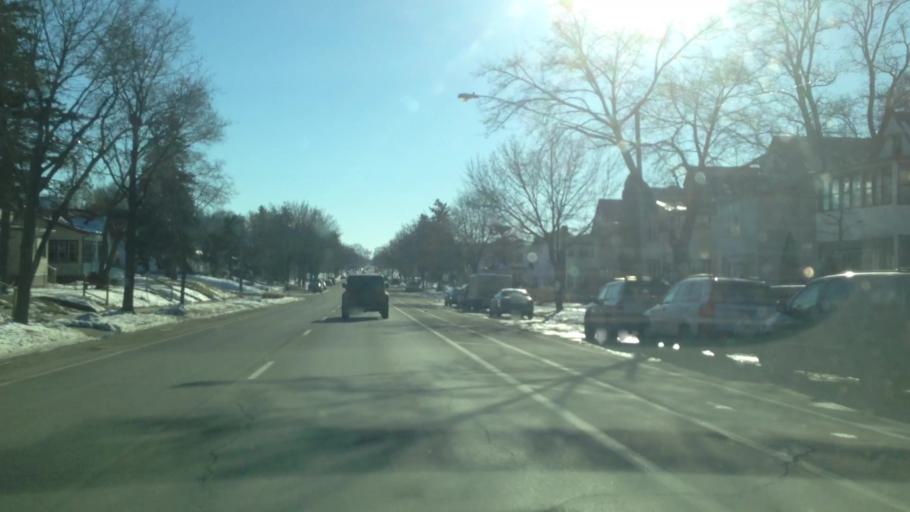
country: US
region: Minnesota
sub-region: Hennepin County
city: Minneapolis
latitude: 44.9315
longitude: -93.2676
